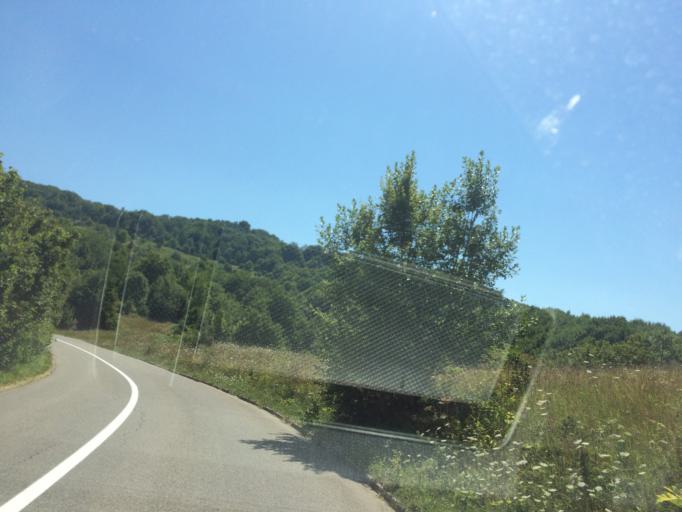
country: ME
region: Opstina Savnik
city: Savnik
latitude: 42.9456
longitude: 19.0757
